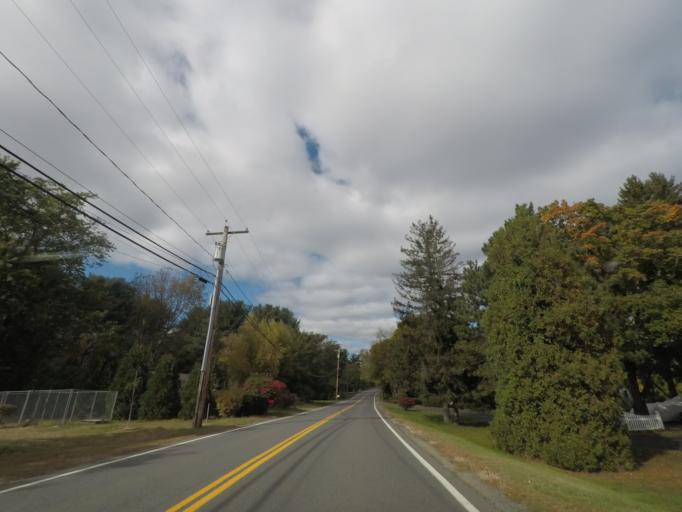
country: US
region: New York
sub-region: Saratoga County
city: Country Knolls
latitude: 42.8387
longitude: -73.7662
